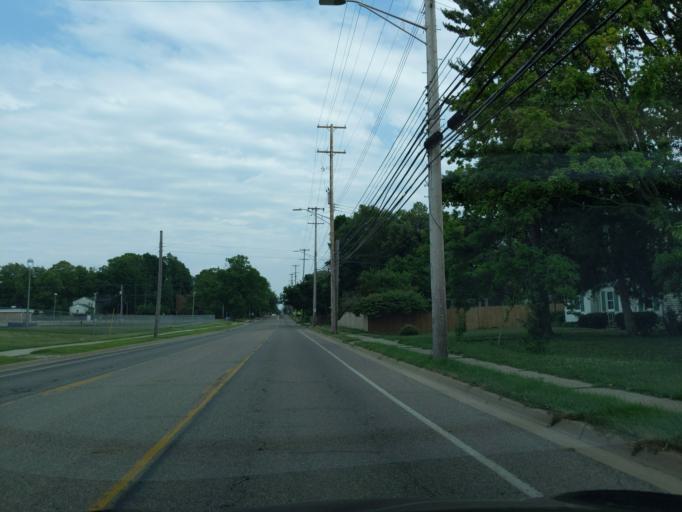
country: US
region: Michigan
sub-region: Ingham County
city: East Lansing
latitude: 42.7406
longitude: -84.4792
